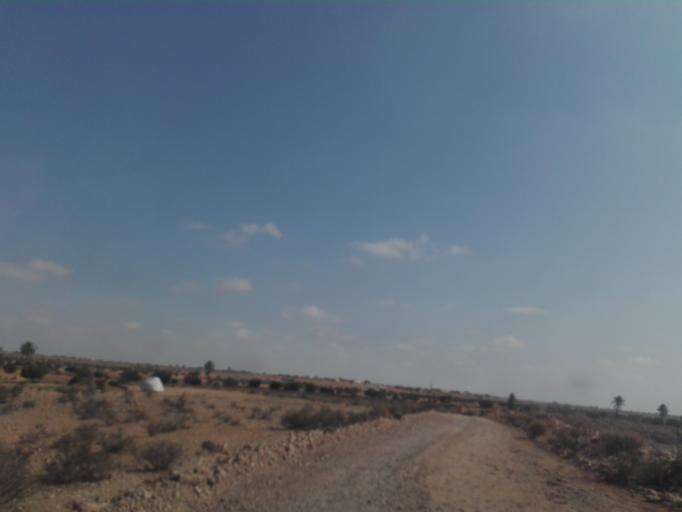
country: TN
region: Madanin
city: Medenine
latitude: 33.4341
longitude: 10.4214
